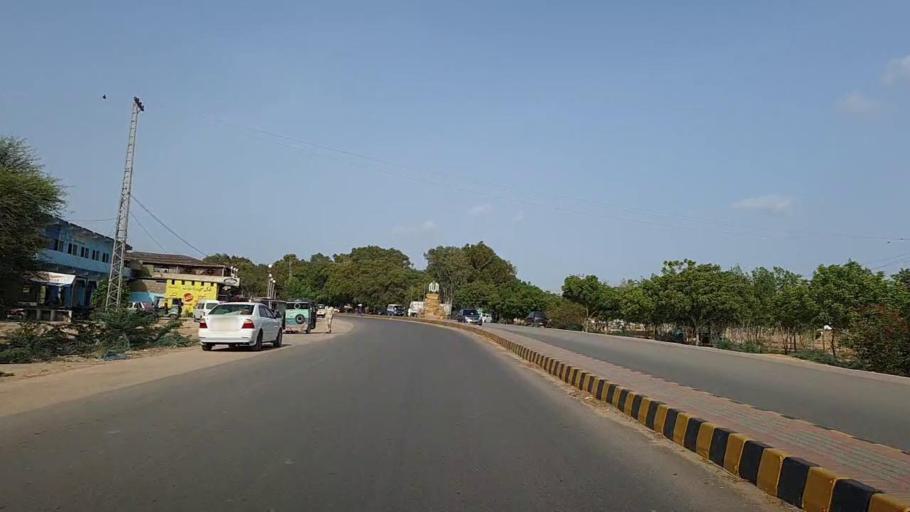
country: PK
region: Sindh
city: Thatta
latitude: 24.7436
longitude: 67.8890
